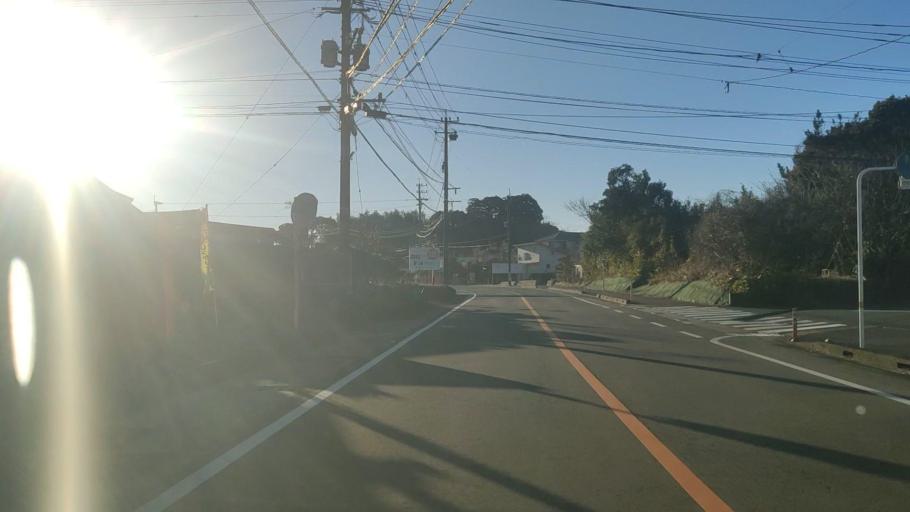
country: JP
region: Miyazaki
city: Miyazaki-shi
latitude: 31.8499
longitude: 131.3533
